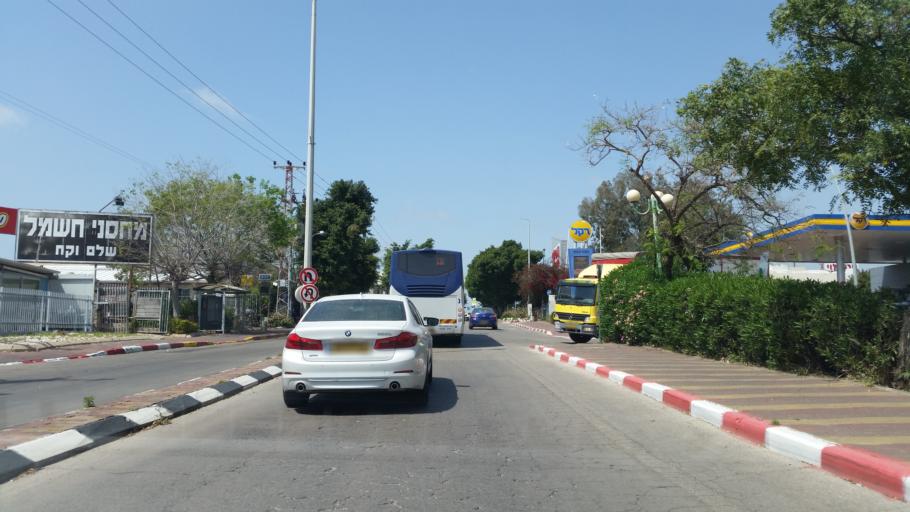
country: IL
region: Central District
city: Ra'anana
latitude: 32.1933
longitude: 34.8809
